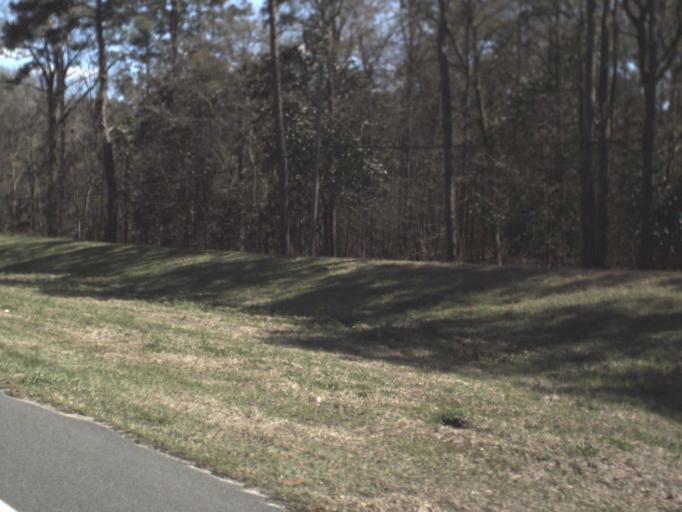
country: US
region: Florida
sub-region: Gadsden County
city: Chattahoochee
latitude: 30.7011
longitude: -84.8286
